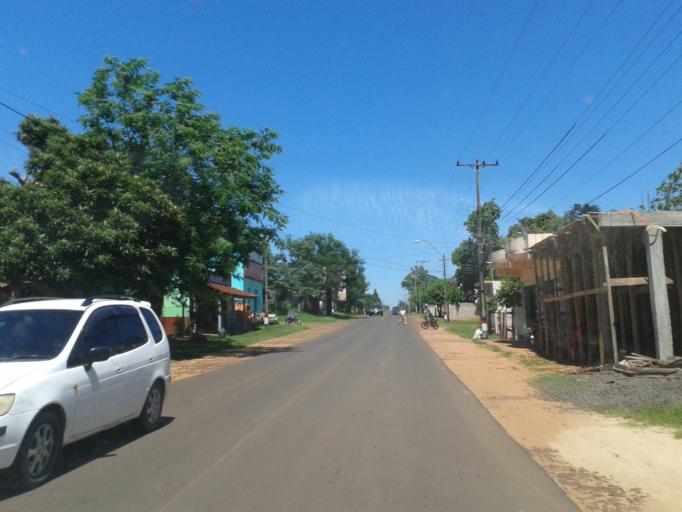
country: PY
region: Misiones
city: Santa Rosa
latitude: -26.8881
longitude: -56.8574
